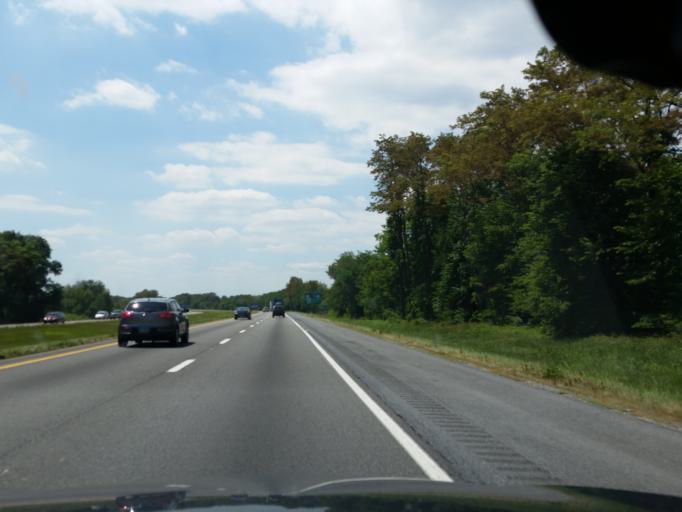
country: US
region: Pennsylvania
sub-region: Cumberland County
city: Schlusser
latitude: 40.2429
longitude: -77.1067
